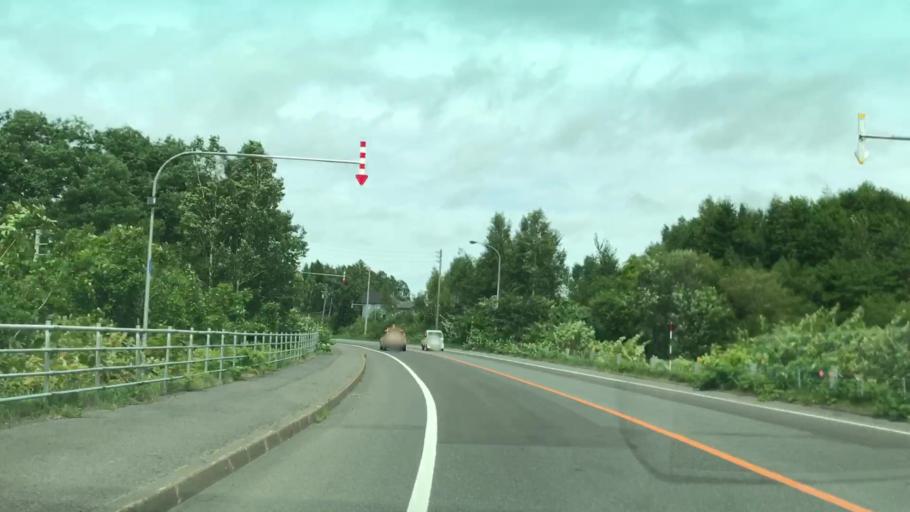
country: JP
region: Hokkaido
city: Niseko Town
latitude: 42.9110
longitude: 140.7533
